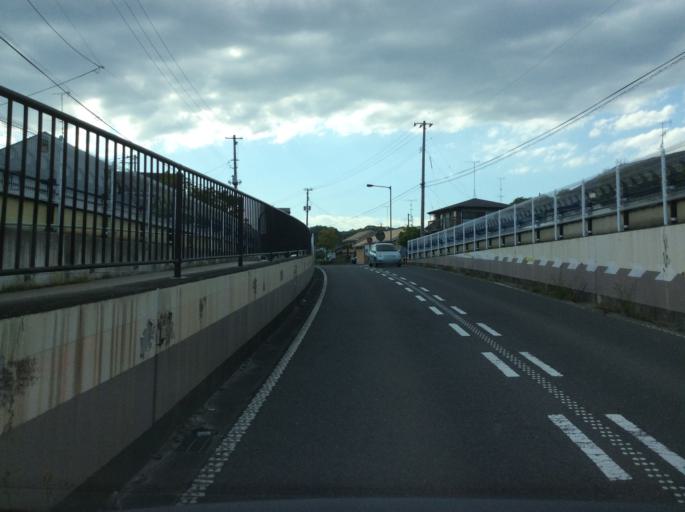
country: JP
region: Fukushima
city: Iwaki
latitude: 36.9591
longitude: 140.8581
